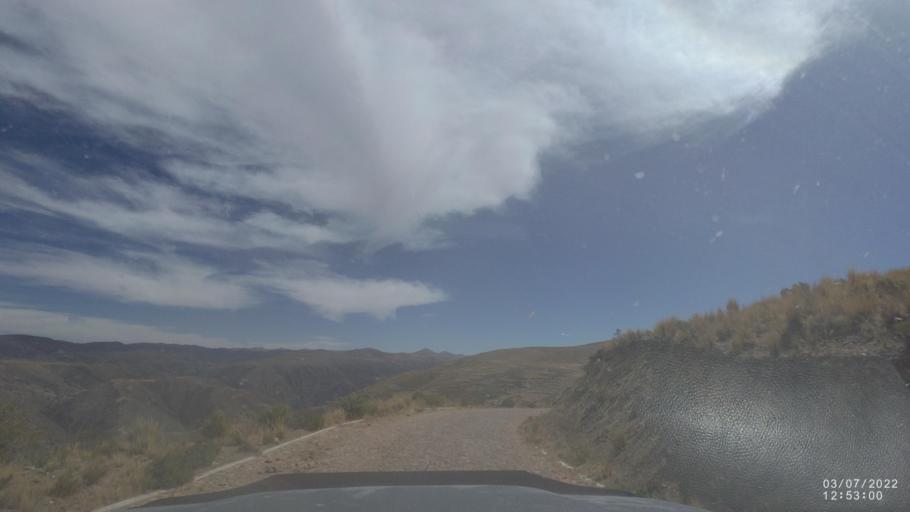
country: BO
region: Cochabamba
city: Irpa Irpa
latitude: -17.7467
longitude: -66.6611
